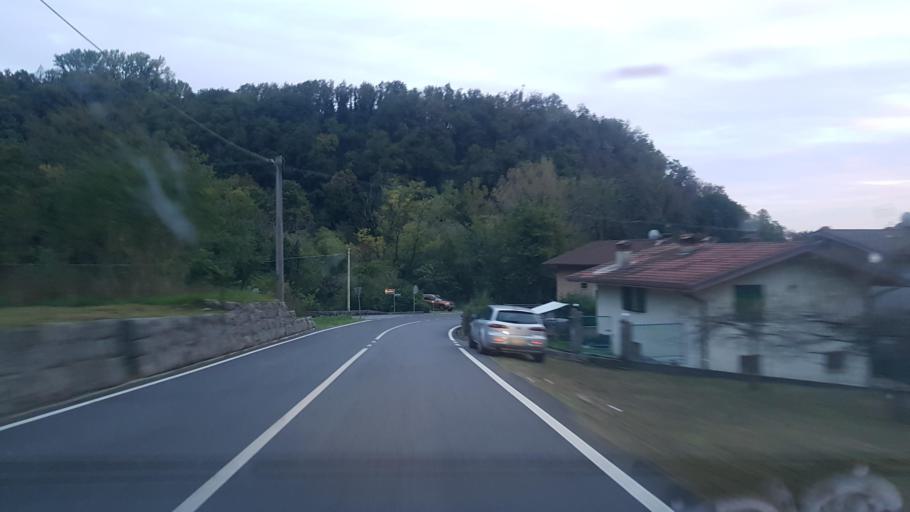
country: IT
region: Friuli Venezia Giulia
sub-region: Provincia di Pordenone
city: Anduins
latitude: 46.2272
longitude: 12.9580
